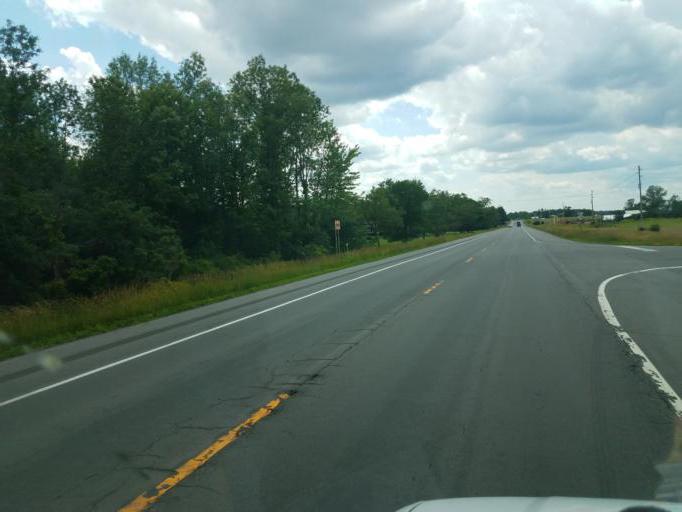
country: US
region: New York
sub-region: Seneca County
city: Waterloo
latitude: 42.9603
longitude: -76.8638
